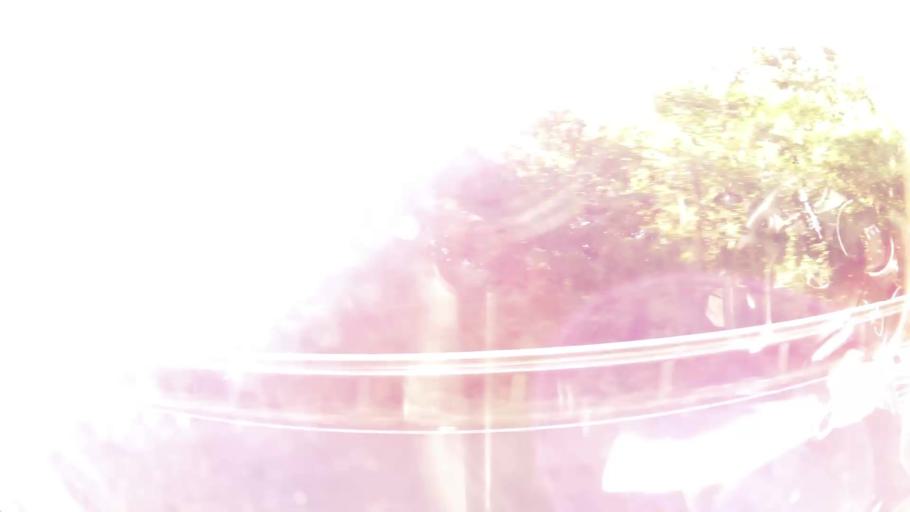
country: CR
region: Guanacaste
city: Belen
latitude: 10.3696
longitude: -85.6343
